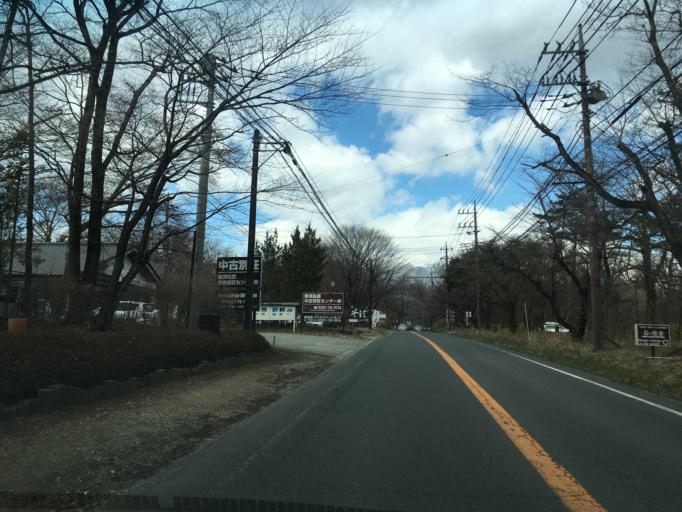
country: JP
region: Tochigi
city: Kuroiso
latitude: 37.0384
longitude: 140.0163
